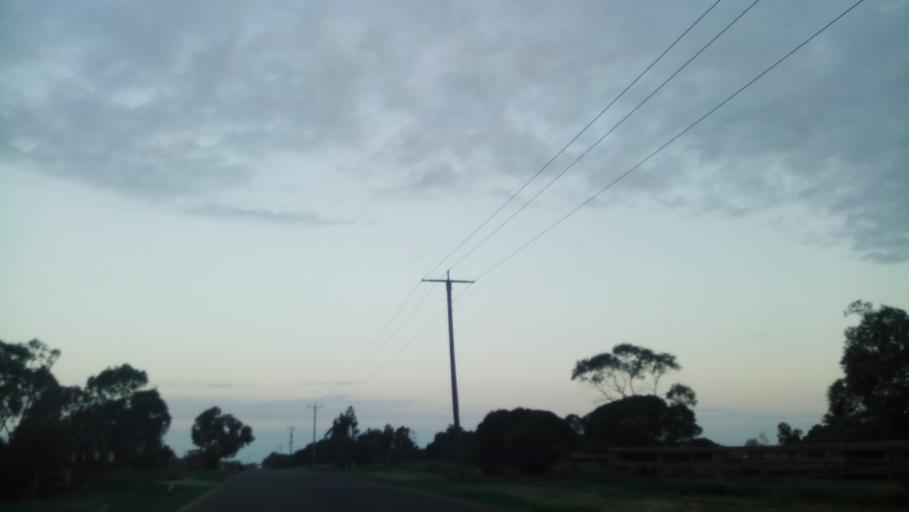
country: AU
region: Victoria
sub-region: Wyndham
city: Point Cook
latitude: -37.9147
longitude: 144.7538
